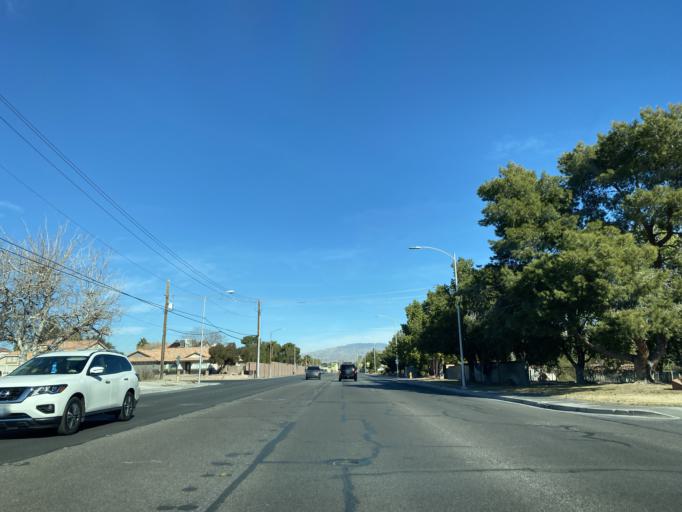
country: US
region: Nevada
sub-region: Clark County
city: Las Vegas
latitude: 36.2128
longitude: -115.2251
